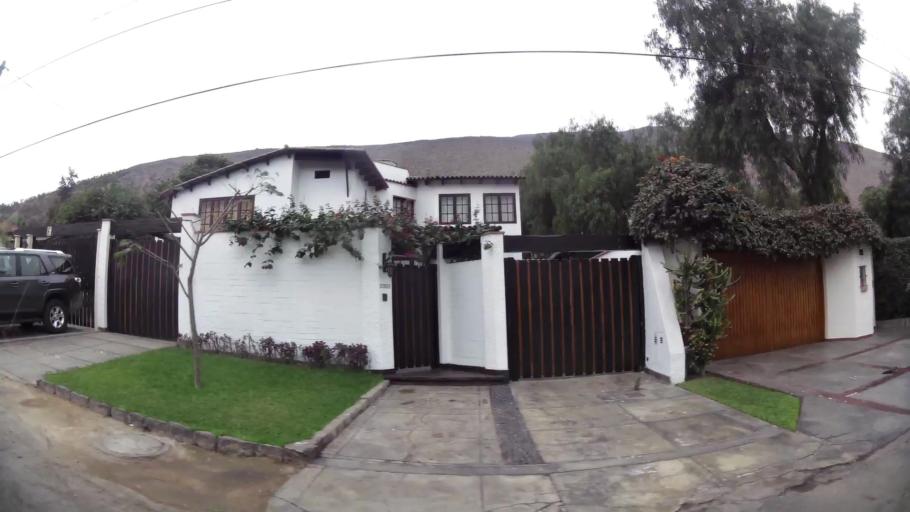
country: PE
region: Lima
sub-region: Lima
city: La Molina
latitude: -12.0878
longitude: -76.9213
